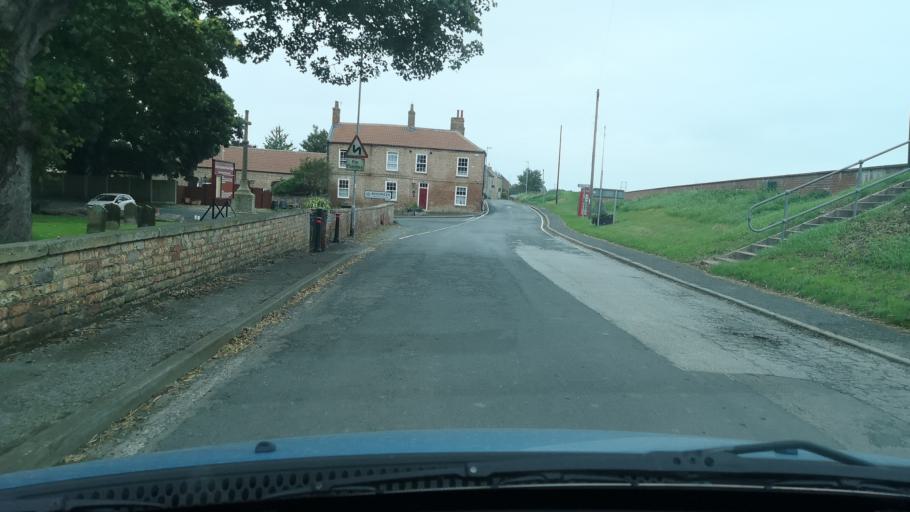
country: GB
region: England
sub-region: East Riding of Yorkshire
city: Laxton
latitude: 53.6947
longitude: -0.7765
